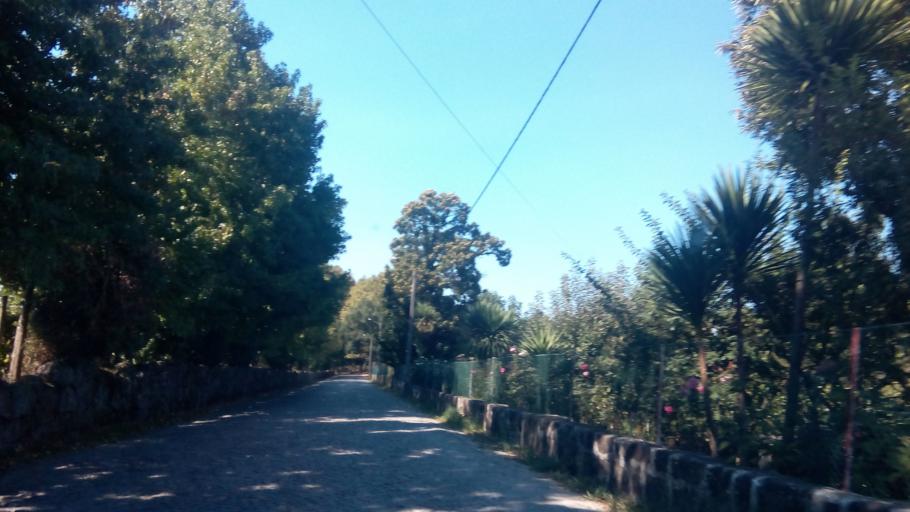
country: PT
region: Porto
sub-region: Penafiel
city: Penafiel
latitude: 41.2089
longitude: -8.2929
